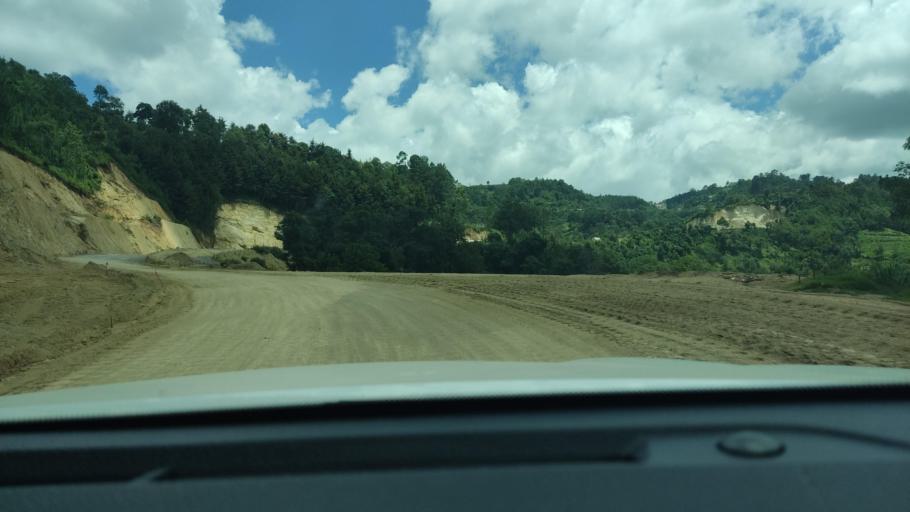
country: GT
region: Chimaltenango
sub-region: Municipio de San Juan Comalapa
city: Comalapa
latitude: 14.7825
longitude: -90.8672
